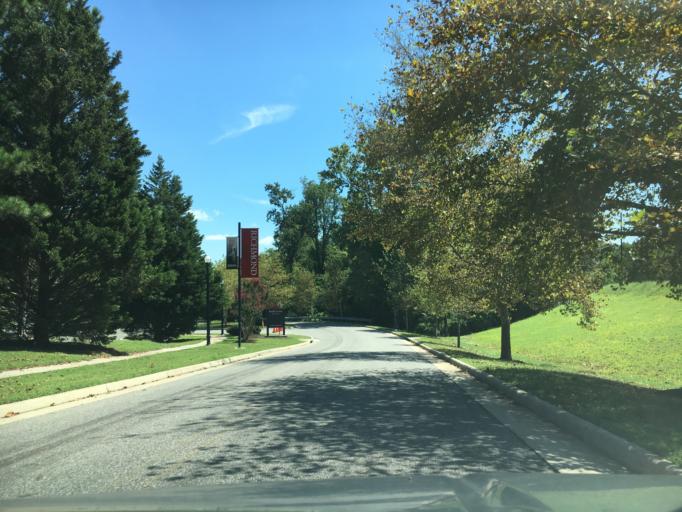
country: US
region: Virginia
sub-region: Henrico County
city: Tuckahoe
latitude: 37.5730
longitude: -77.5445
